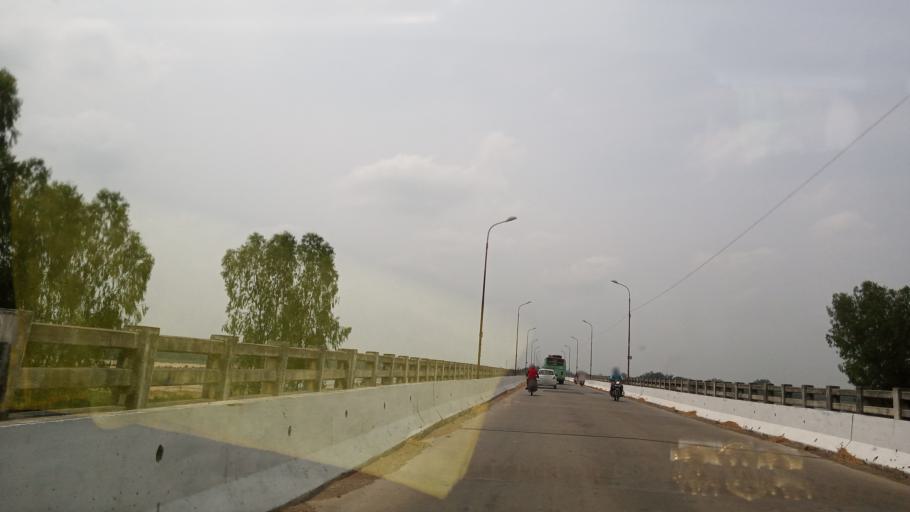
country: IN
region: Tamil Nadu
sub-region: Thanjavur
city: Kumbakonam
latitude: 11.0541
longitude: 79.3596
